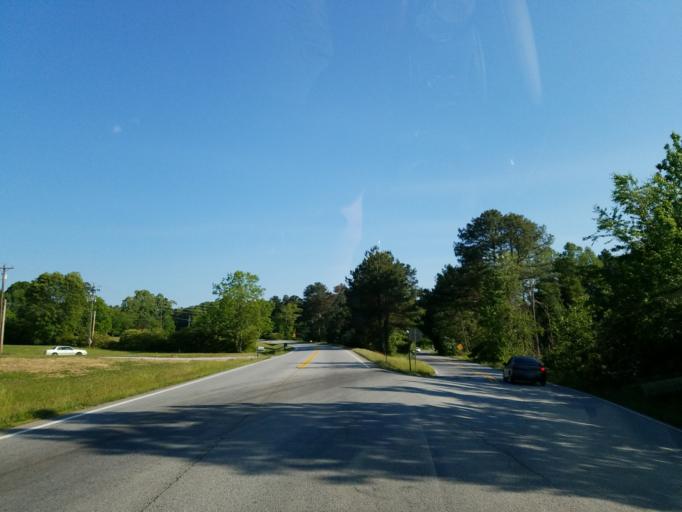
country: US
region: Georgia
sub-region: Carroll County
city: Villa Rica
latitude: 33.7773
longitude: -84.9643
